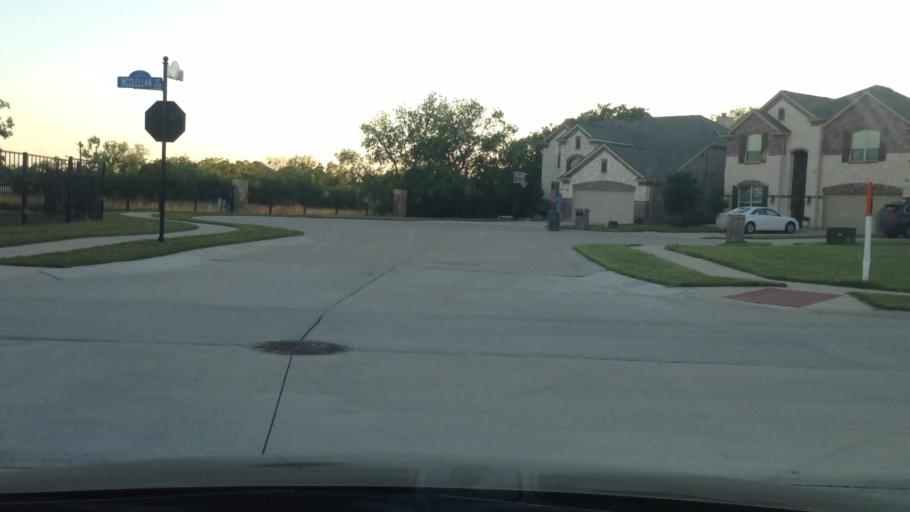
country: US
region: Texas
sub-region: Denton County
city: Little Elm
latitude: 33.1374
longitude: -96.9329
